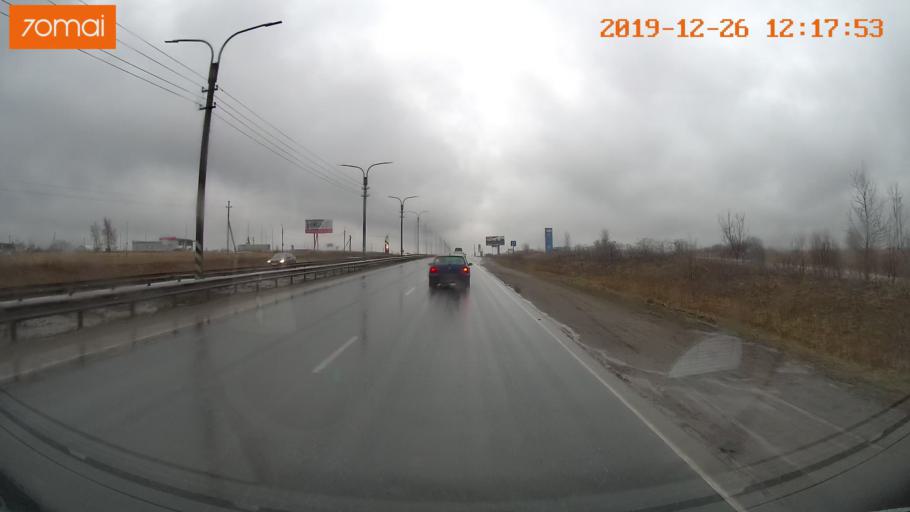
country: RU
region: Vologda
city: Tonshalovo
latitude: 59.1842
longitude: 37.9431
